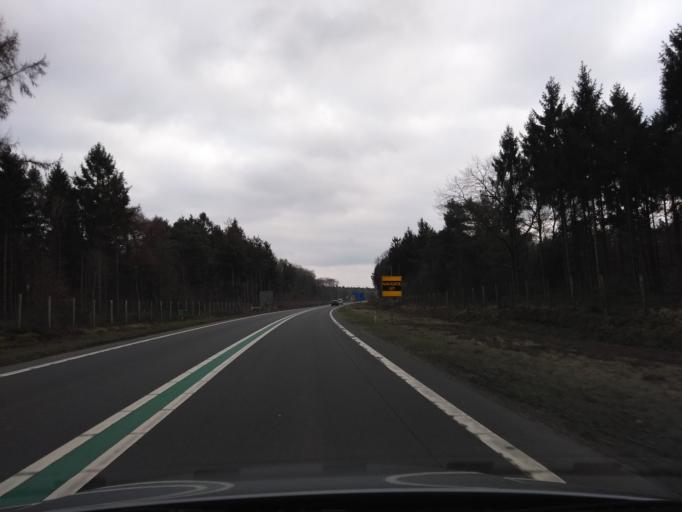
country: NL
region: Overijssel
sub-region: Gemeente Hardenberg
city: Hardenberg
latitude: 52.5584
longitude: 6.5320
